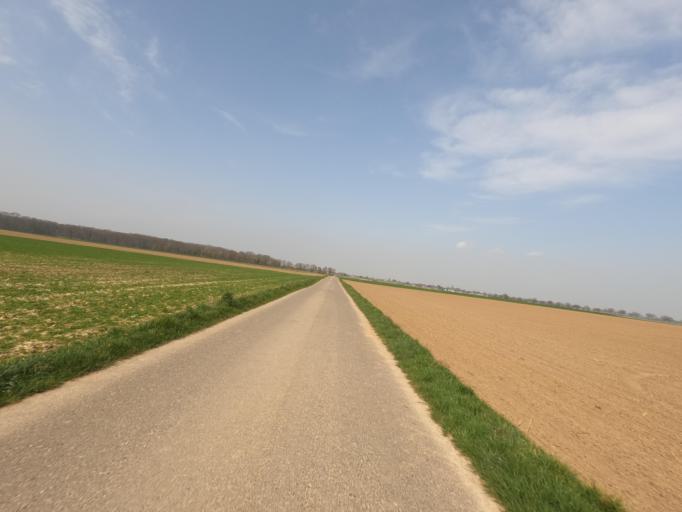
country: DE
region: North Rhine-Westphalia
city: Erkelenz
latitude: 51.0451
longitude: 6.3416
